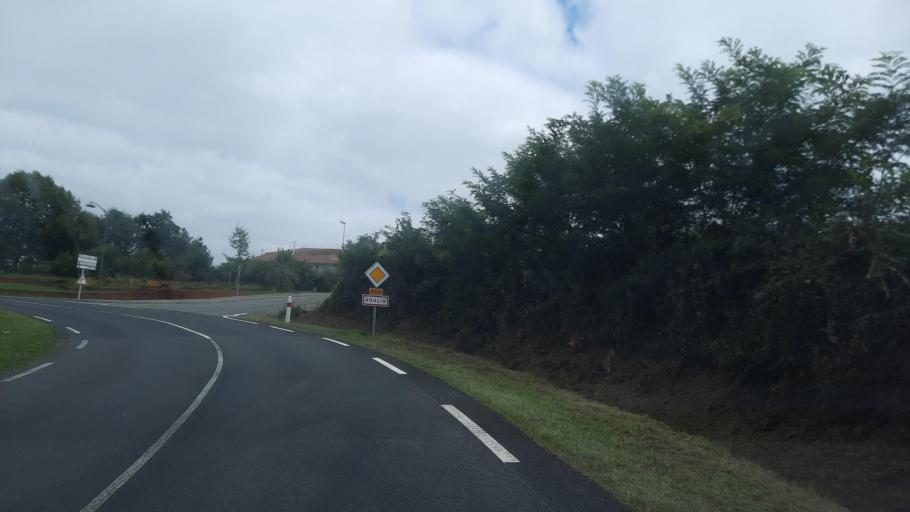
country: FR
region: Midi-Pyrenees
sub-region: Departement des Hautes-Pyrenees
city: Orleix
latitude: 43.2531
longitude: 0.1345
